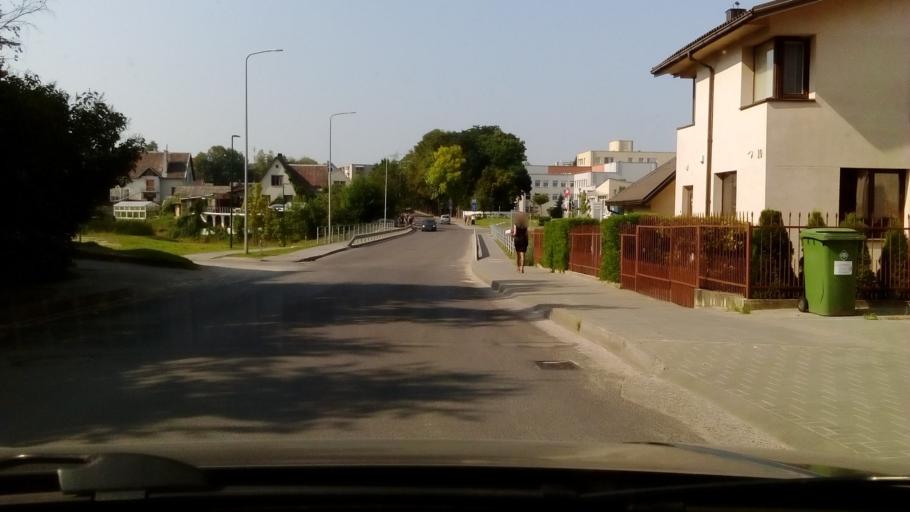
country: LT
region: Alytaus apskritis
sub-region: Alytus
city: Alytus
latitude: 54.3979
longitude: 24.0433
